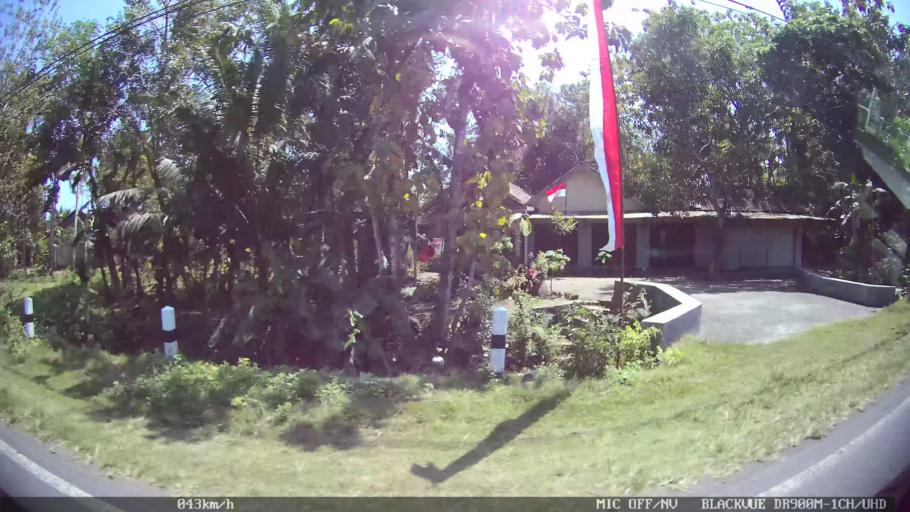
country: ID
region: Daerah Istimewa Yogyakarta
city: Srandakan
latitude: -7.9505
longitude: 110.2170
